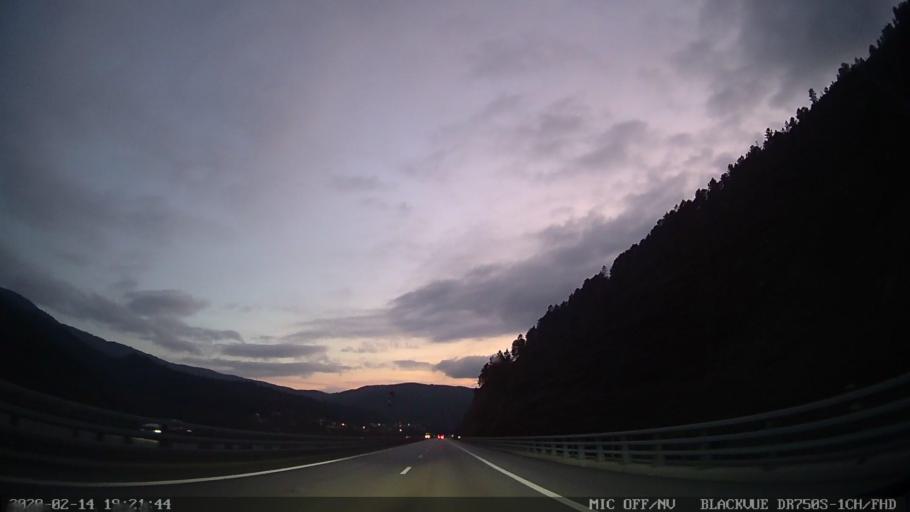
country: PT
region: Porto
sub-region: Baiao
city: Valadares
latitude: 41.2613
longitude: -7.9450
